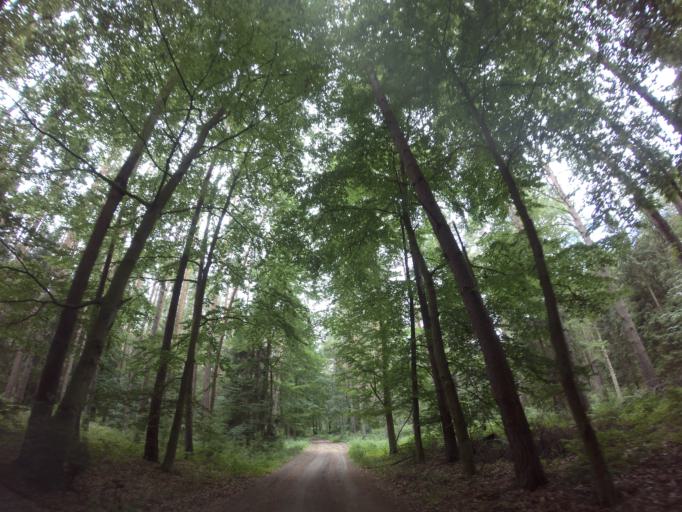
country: PL
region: Lubusz
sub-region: Powiat strzelecko-drezdenecki
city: Strzelce Krajenskie
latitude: 52.9314
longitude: 15.6093
